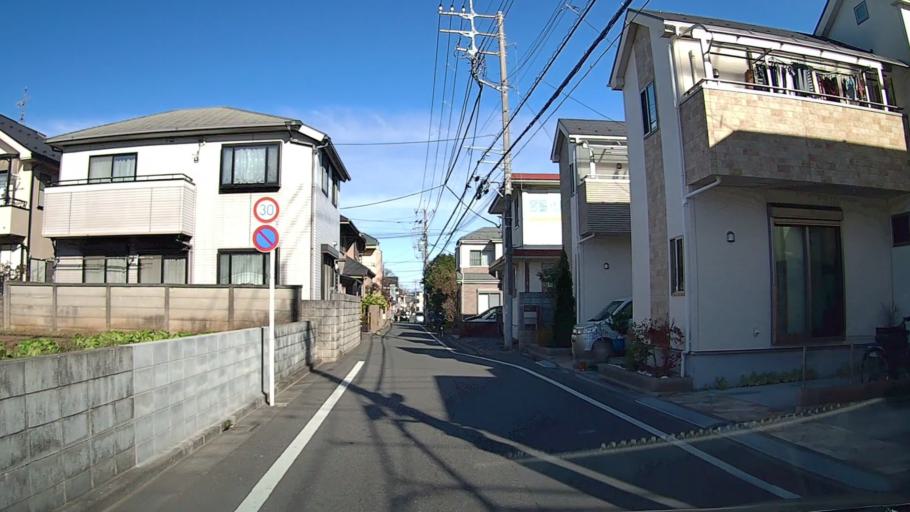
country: JP
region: Saitama
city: Wako
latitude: 35.7558
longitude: 139.6123
